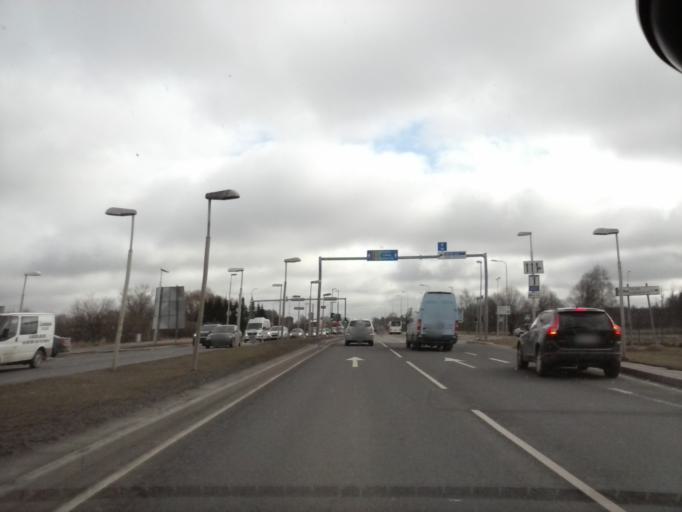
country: EE
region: Harju
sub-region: Tallinna linn
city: Tallinn
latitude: 59.4126
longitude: 24.8007
